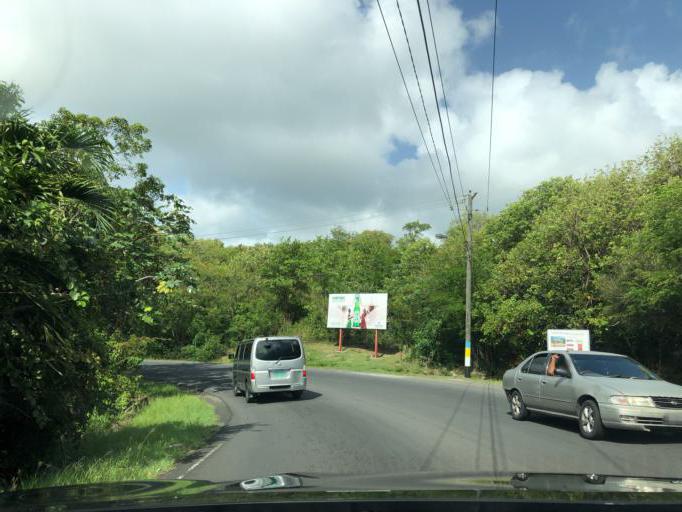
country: LC
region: Dennery Quarter
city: Dennery
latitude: 13.9214
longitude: -60.8975
